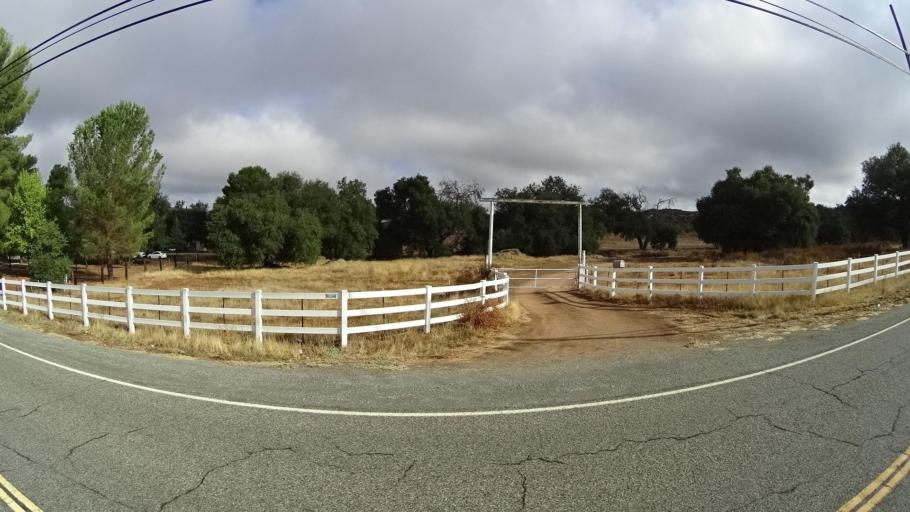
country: MX
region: Baja California
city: Tecate
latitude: 32.6044
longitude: -116.6084
